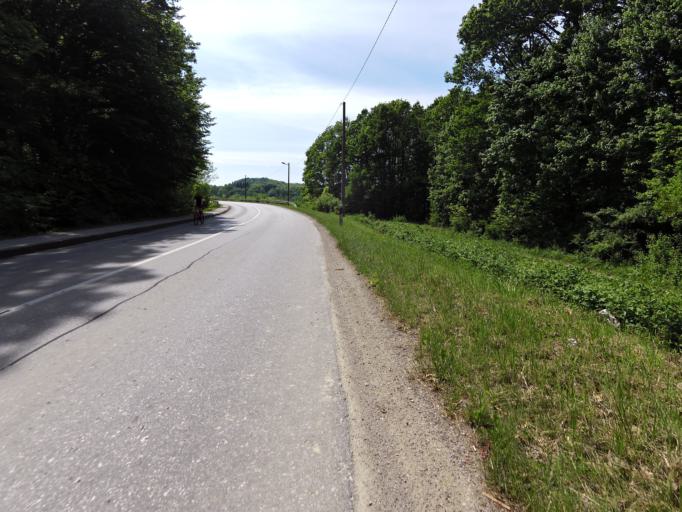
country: HR
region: Karlovacka
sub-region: Grad Karlovac
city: Karlovac
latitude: 45.5476
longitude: 15.5366
